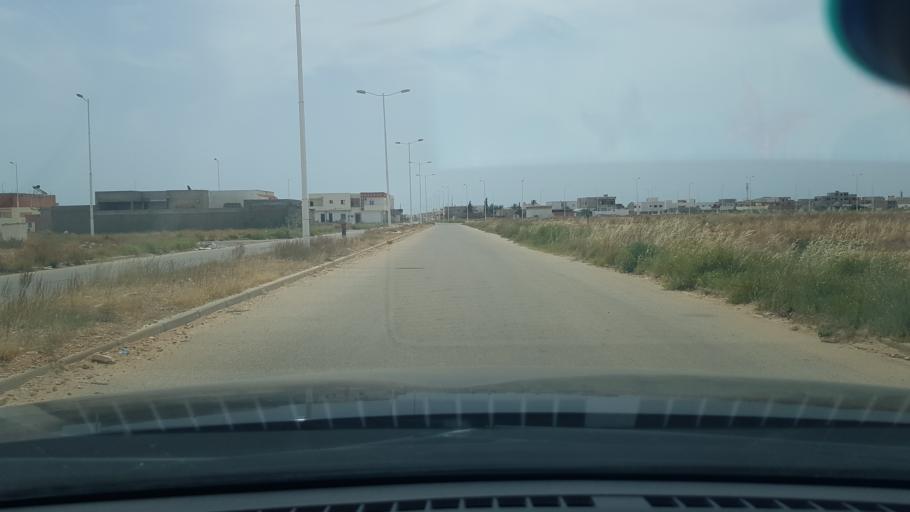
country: TN
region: Safaqis
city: Al Qarmadah
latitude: 34.8315
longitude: 10.7480
